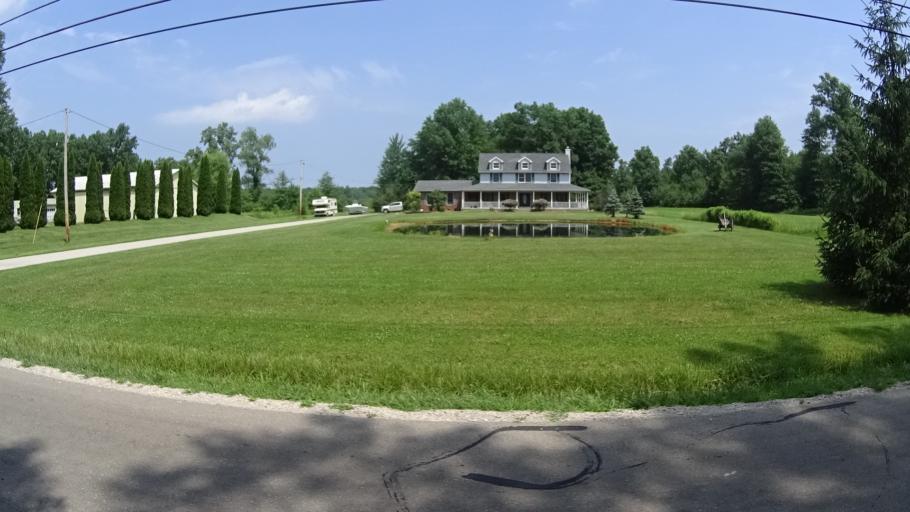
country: US
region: Ohio
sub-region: Lorain County
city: Vermilion
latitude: 41.3865
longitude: -82.3928
